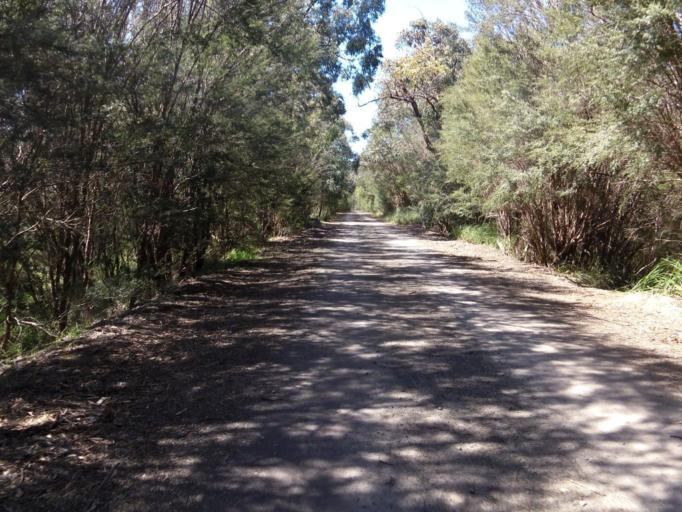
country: AU
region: Victoria
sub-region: Latrobe
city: Moe
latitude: -38.1714
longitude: 146.2976
